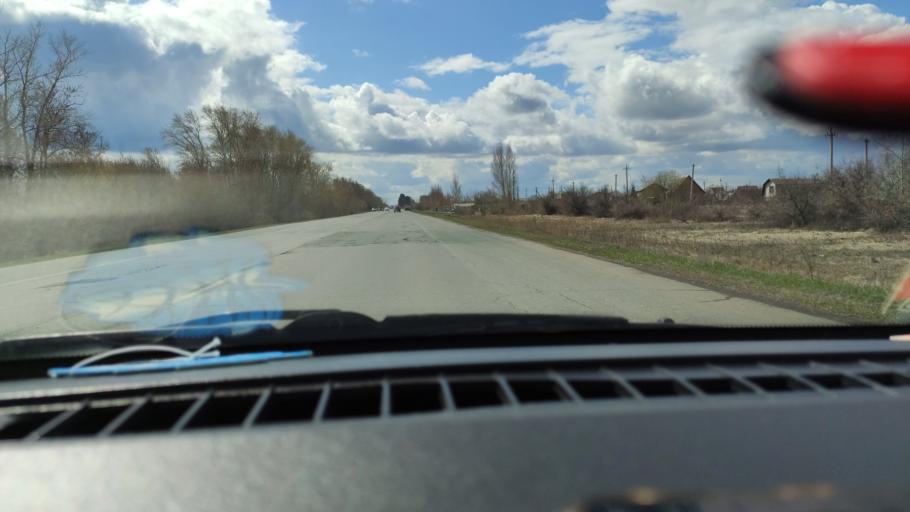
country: RU
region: Samara
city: Tol'yatti
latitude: 53.7008
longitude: 49.4207
